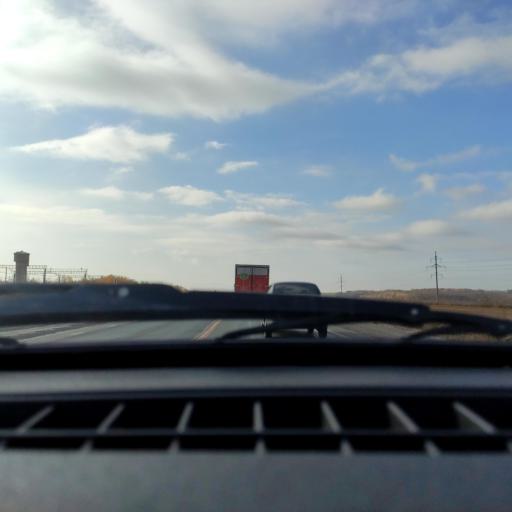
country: RU
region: Bashkortostan
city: Kabakovo
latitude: 54.7076
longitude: 56.2230
